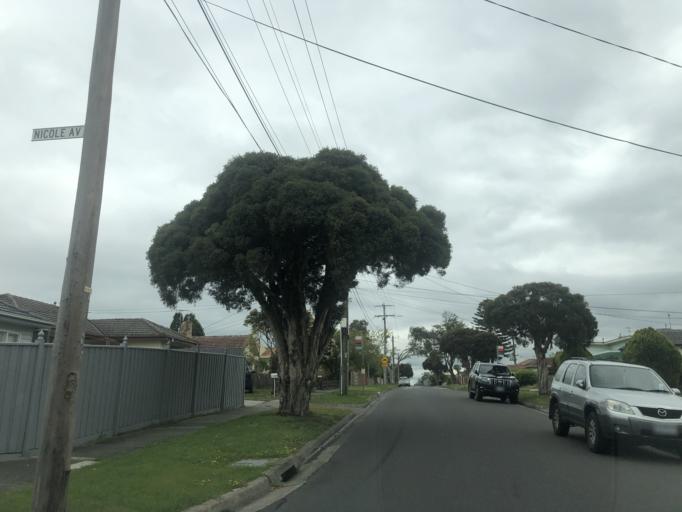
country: AU
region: Victoria
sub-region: Greater Dandenong
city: Dandenong North
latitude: -37.9692
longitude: 145.2170
